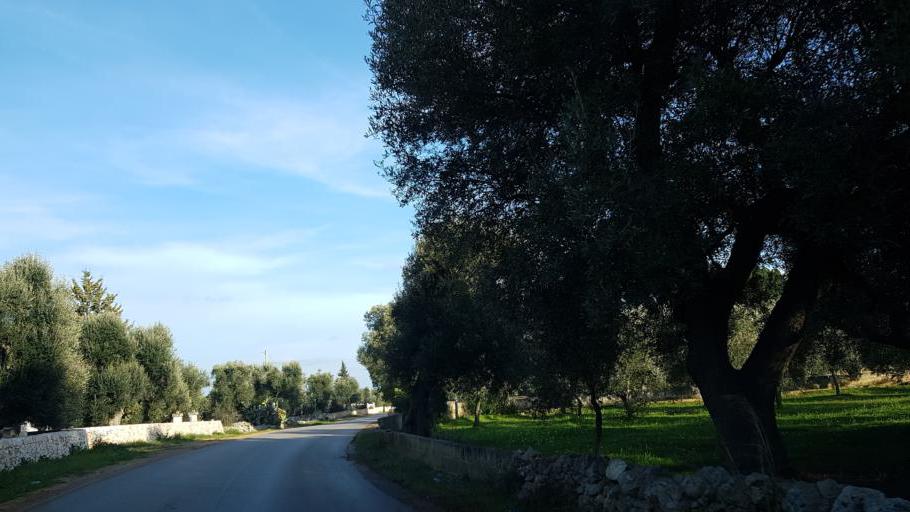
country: IT
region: Apulia
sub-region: Provincia di Brindisi
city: Carovigno
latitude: 40.7060
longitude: 17.7032
